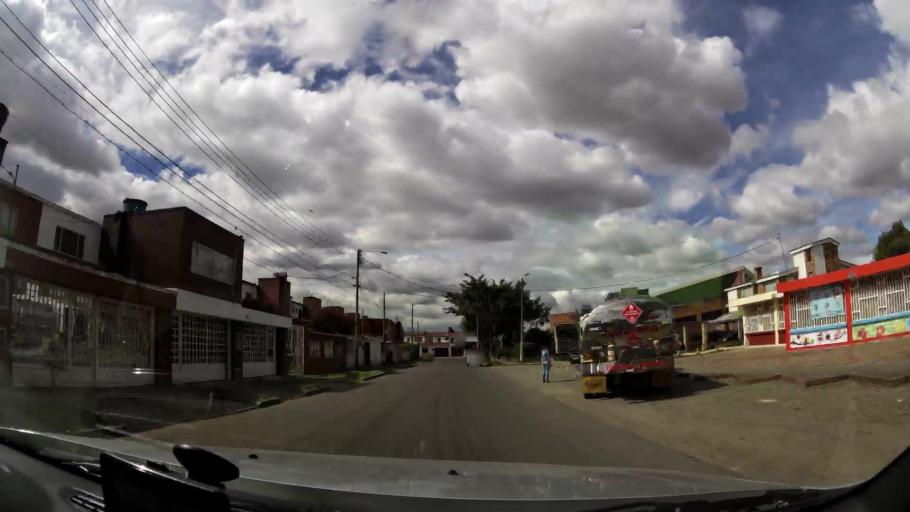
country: CO
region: Bogota D.C.
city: Bogota
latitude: 4.6260
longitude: -74.1282
